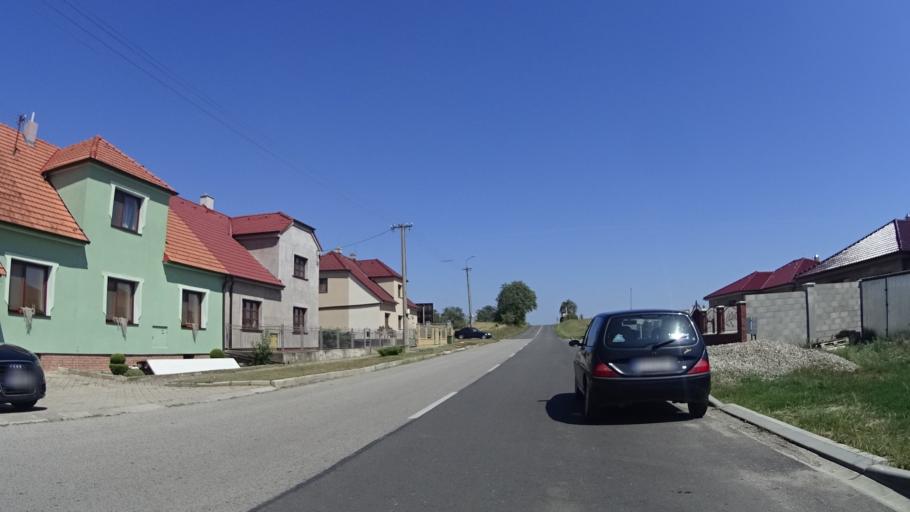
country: SK
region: Trnavsky
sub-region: Okres Skalica
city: Skalica
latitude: 48.8509
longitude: 17.2383
